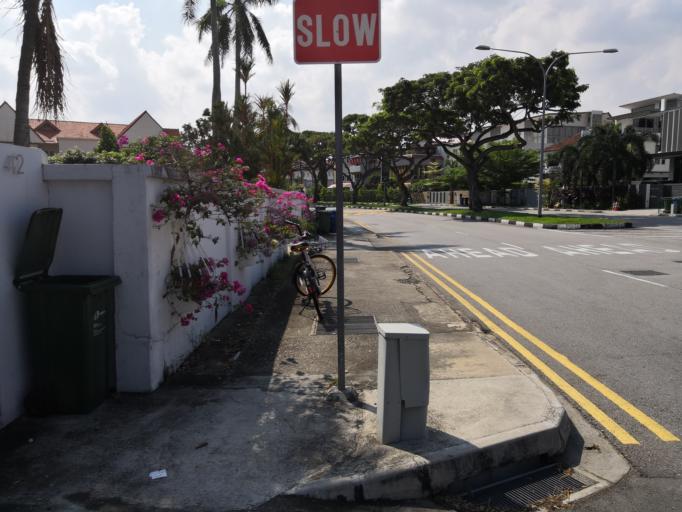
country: SG
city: Singapore
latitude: 1.3156
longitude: 103.9186
